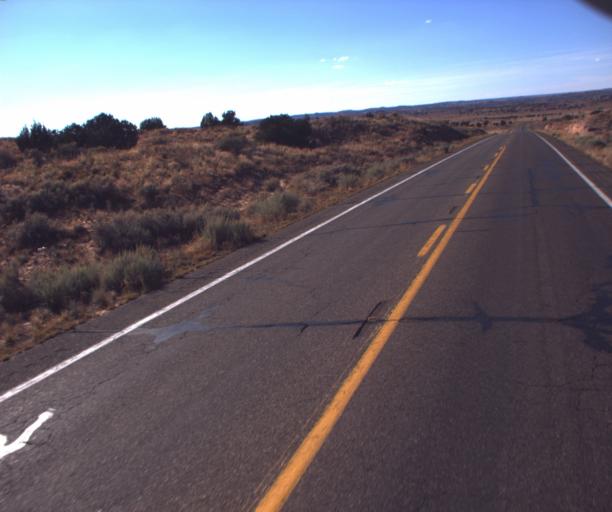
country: US
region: Arizona
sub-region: Coconino County
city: Kaibito
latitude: 36.5791
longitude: -111.1350
